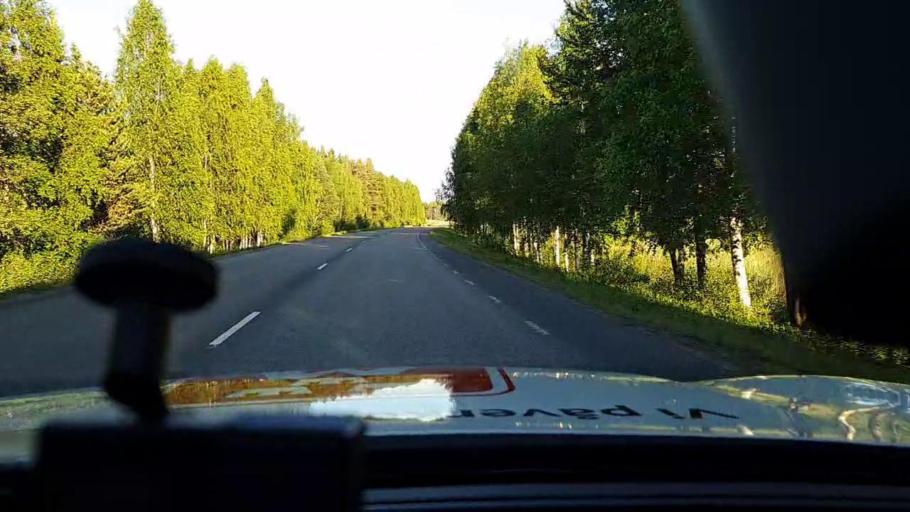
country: SE
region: Norrbotten
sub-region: Lulea Kommun
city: Lulea
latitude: 65.6114
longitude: 22.1630
